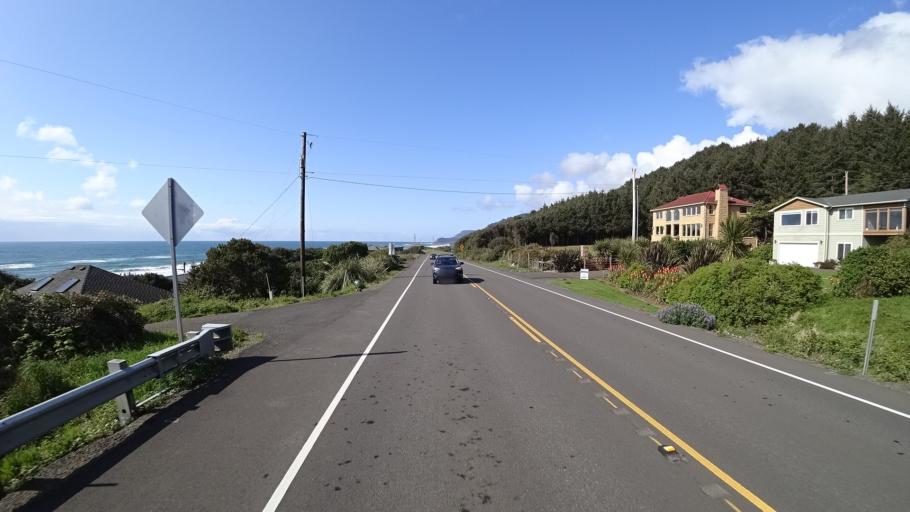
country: US
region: Oregon
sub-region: Lincoln County
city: Waldport
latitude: 44.2162
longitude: -124.1135
